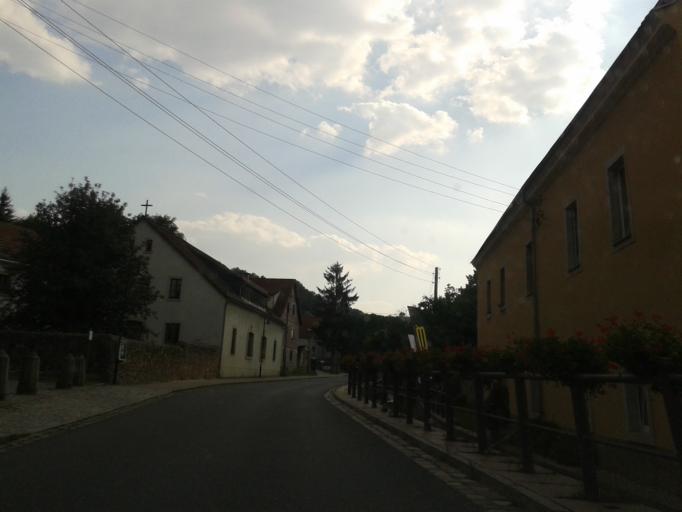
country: DE
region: Saxony
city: Radebeul
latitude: 51.0853
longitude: 13.6275
